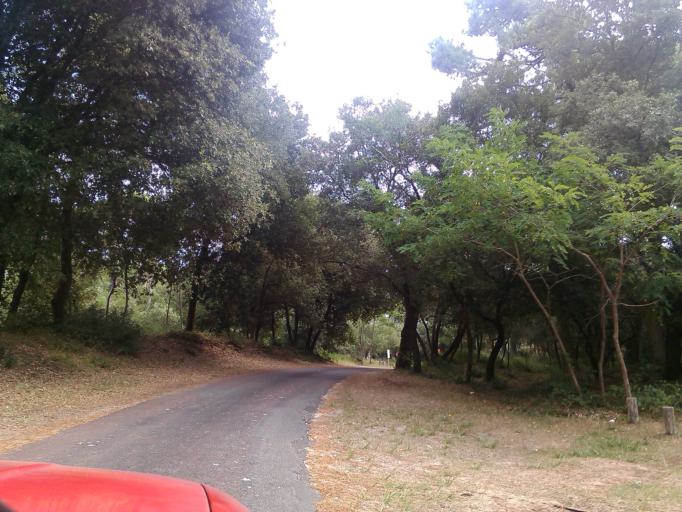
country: FR
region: Poitou-Charentes
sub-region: Departement de la Charente-Maritime
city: Saint-Trojan-les-Bains
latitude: 45.7903
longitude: -1.2057
